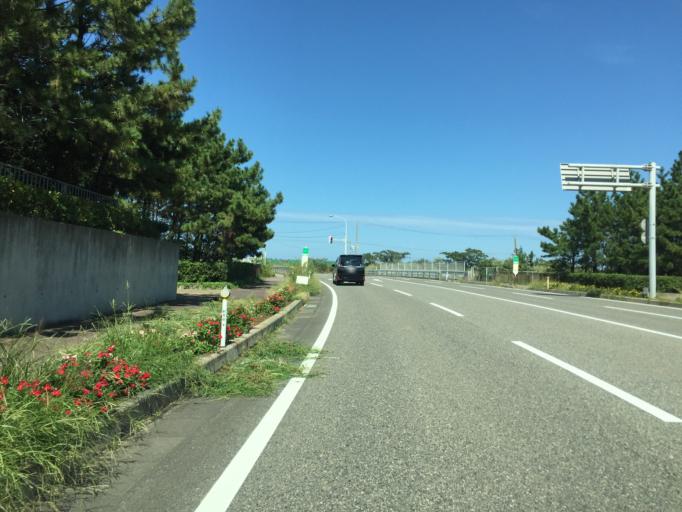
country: JP
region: Niigata
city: Niigata-shi
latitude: 37.9418
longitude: 139.0584
